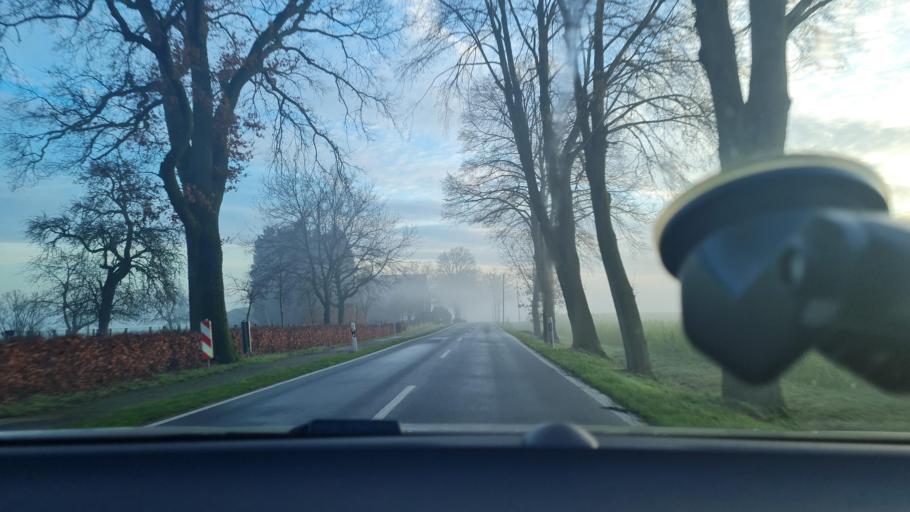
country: DE
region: North Rhine-Westphalia
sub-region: Regierungsbezirk Dusseldorf
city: Hunxe
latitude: 51.6937
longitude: 6.7847
